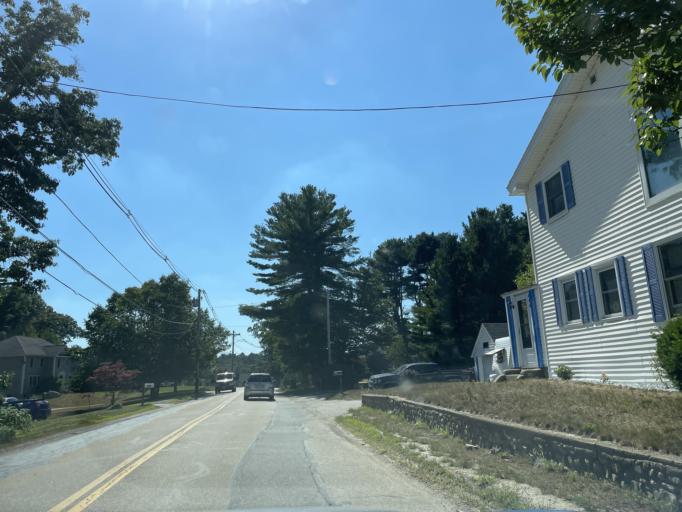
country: US
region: Massachusetts
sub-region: Worcester County
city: East Douglas
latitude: 42.0746
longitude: -71.6974
